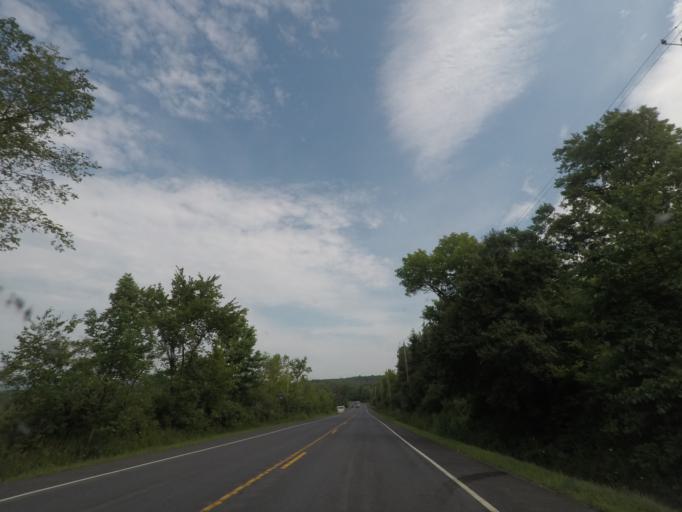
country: US
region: New York
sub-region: Rensselaer County
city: Poestenkill
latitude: 42.7202
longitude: -73.5561
